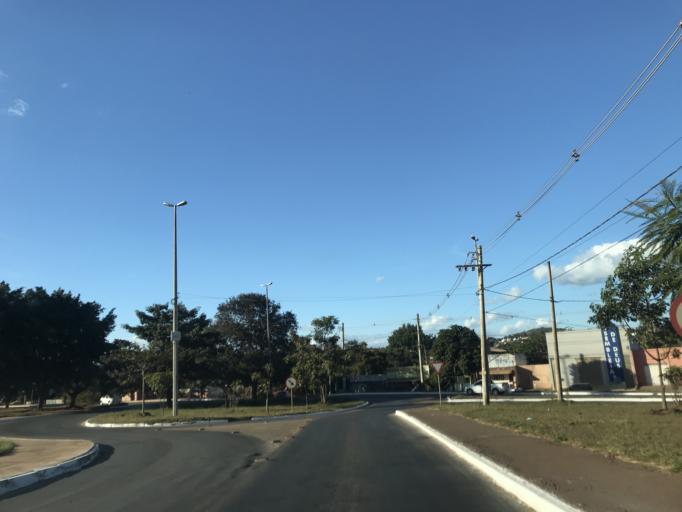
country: BR
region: Federal District
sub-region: Brasilia
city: Brasilia
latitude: -15.8887
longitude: -47.7802
